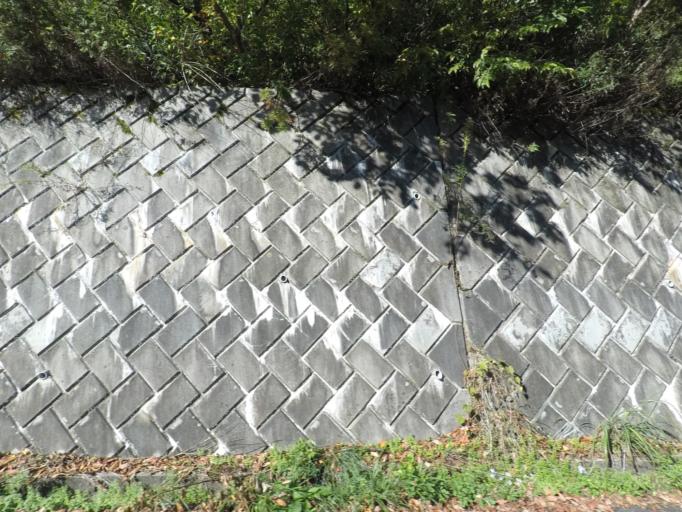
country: JP
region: Nagano
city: Tatsuno
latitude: 35.9847
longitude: 137.7681
